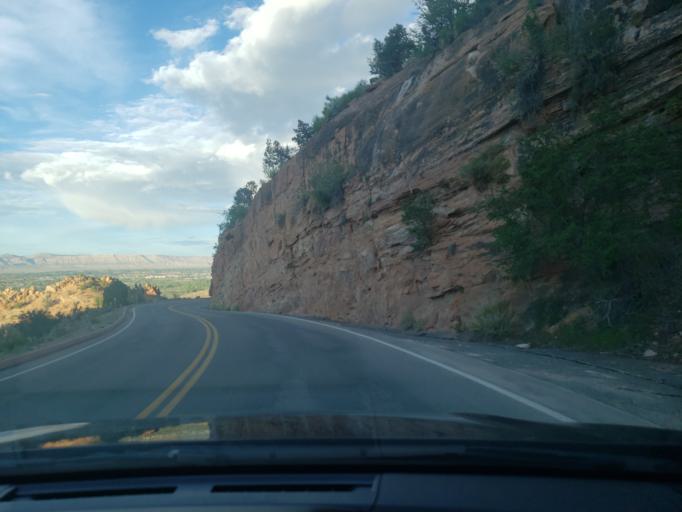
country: US
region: Colorado
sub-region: Mesa County
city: Fruita
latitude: 39.1149
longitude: -108.7267
